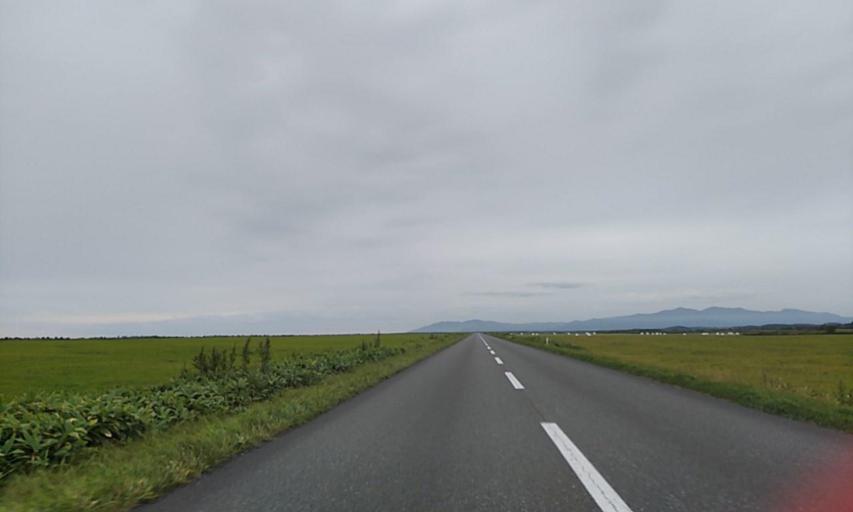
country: JP
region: Hokkaido
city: Makubetsu
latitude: 45.2037
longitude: 142.2969
